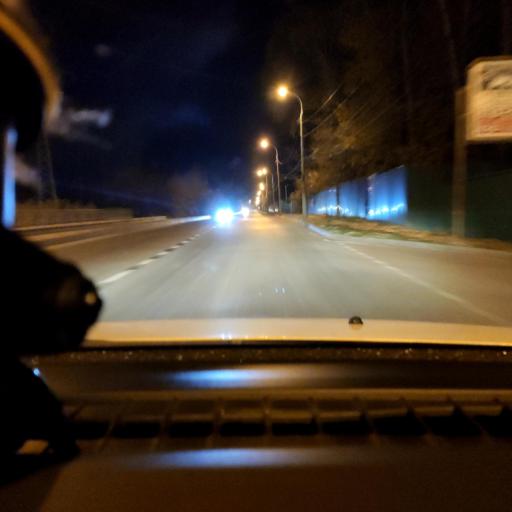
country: RU
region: Samara
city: Rozhdestveno
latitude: 53.1567
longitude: 50.0717
